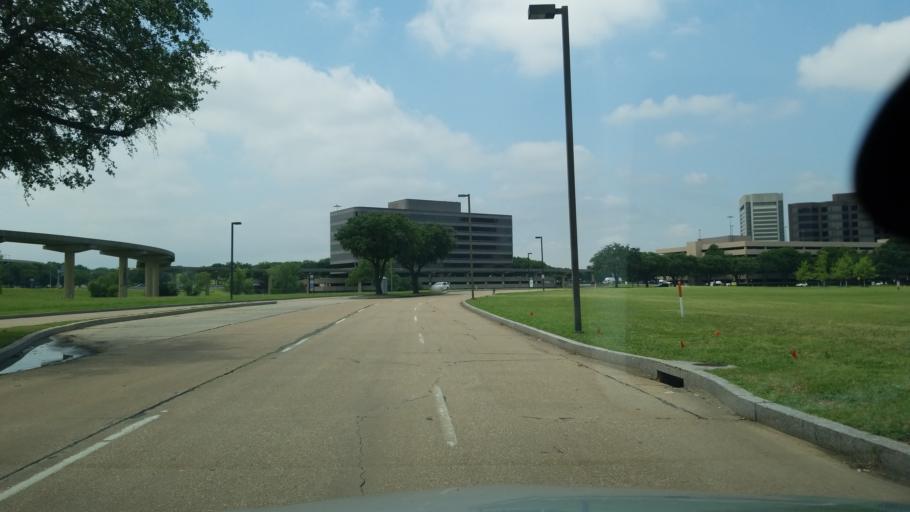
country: US
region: Texas
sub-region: Dallas County
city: Irving
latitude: 32.8611
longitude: -96.9312
